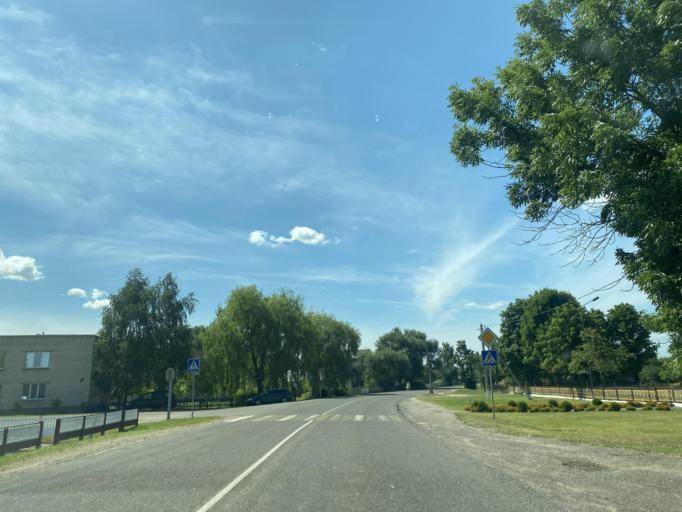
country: BY
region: Brest
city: Ivanava
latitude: 52.1865
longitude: 25.6093
